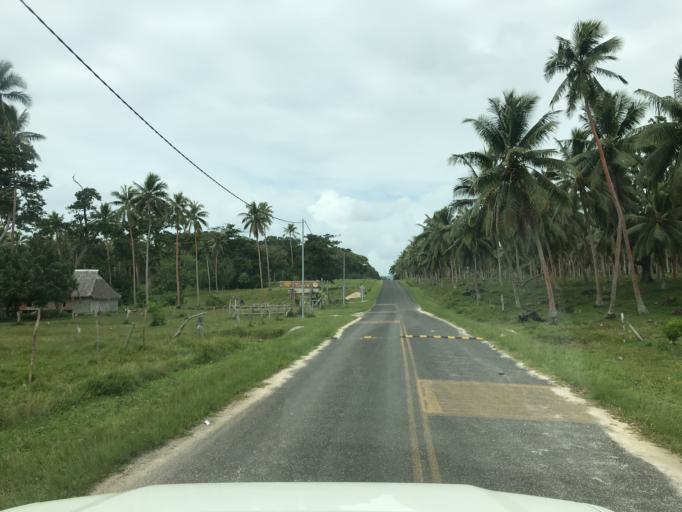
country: VU
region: Sanma
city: Port-Olry
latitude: -15.0465
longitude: 167.0719
